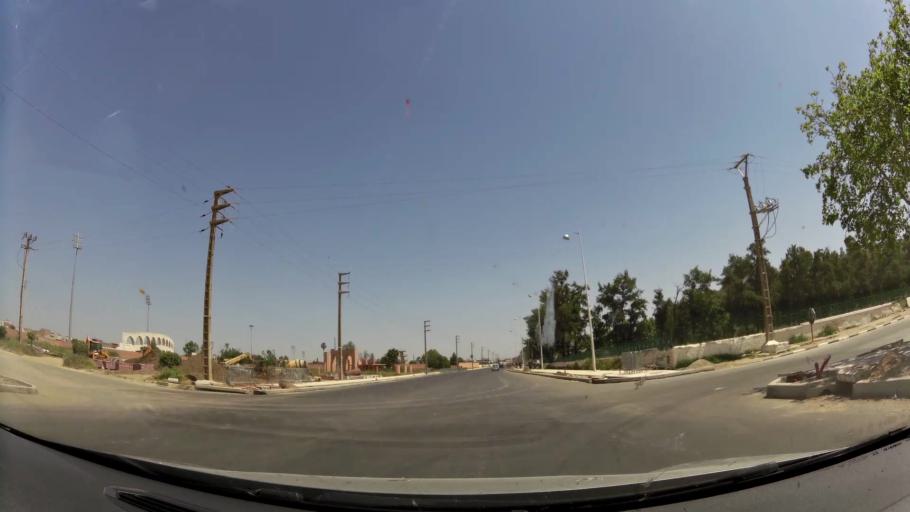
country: MA
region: Rabat-Sale-Zemmour-Zaer
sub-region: Khemisset
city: Khemisset
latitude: 33.8161
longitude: -6.0747
